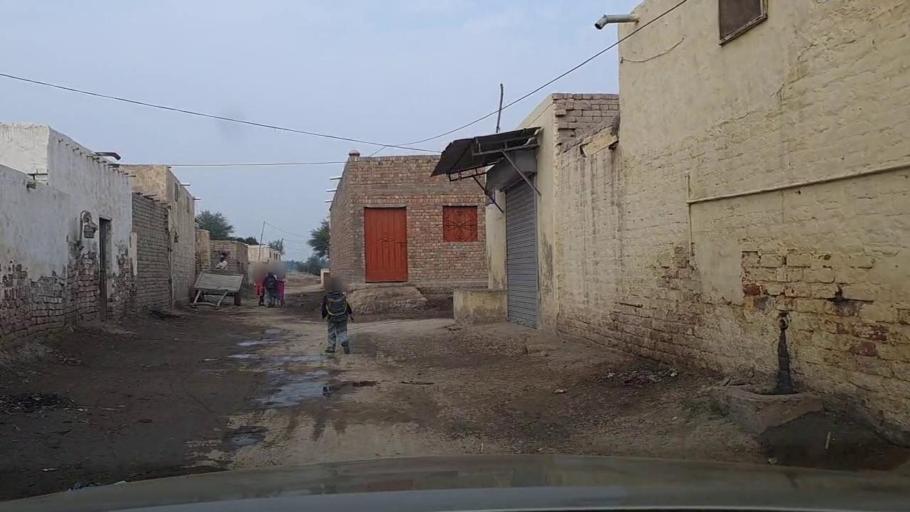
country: PK
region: Sindh
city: Sanghar
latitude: 26.1407
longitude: 68.9637
